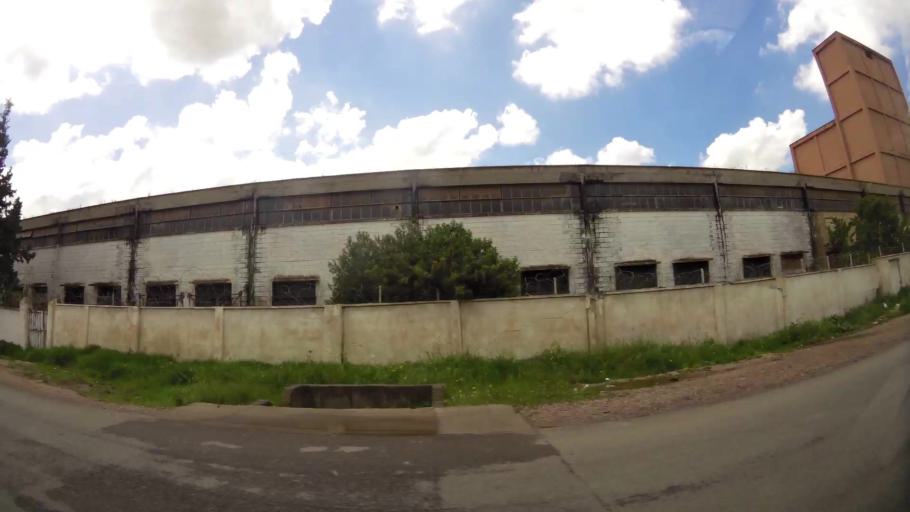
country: MA
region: Chaouia-Ouardigha
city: Nouaseur
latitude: 33.3848
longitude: -7.5752
